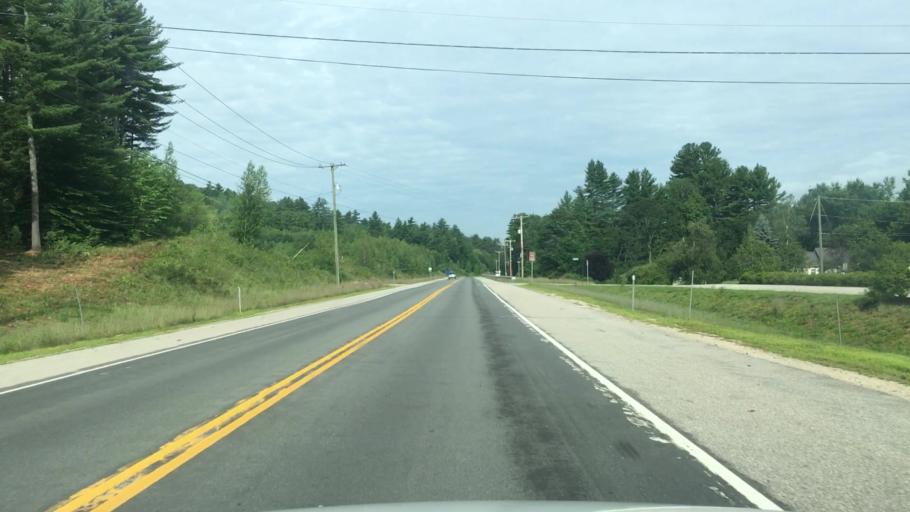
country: US
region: New Hampshire
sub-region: Carroll County
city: Tamworth
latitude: 43.8201
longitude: -71.2120
